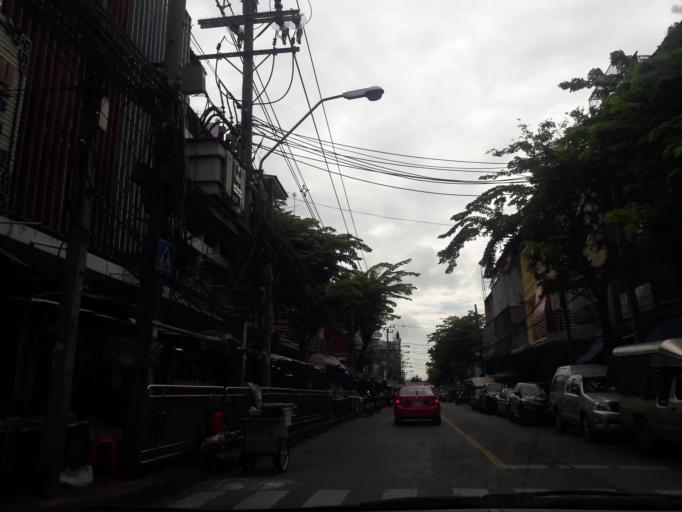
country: TH
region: Bangkok
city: Thon Buri
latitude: 13.7252
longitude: 100.4944
